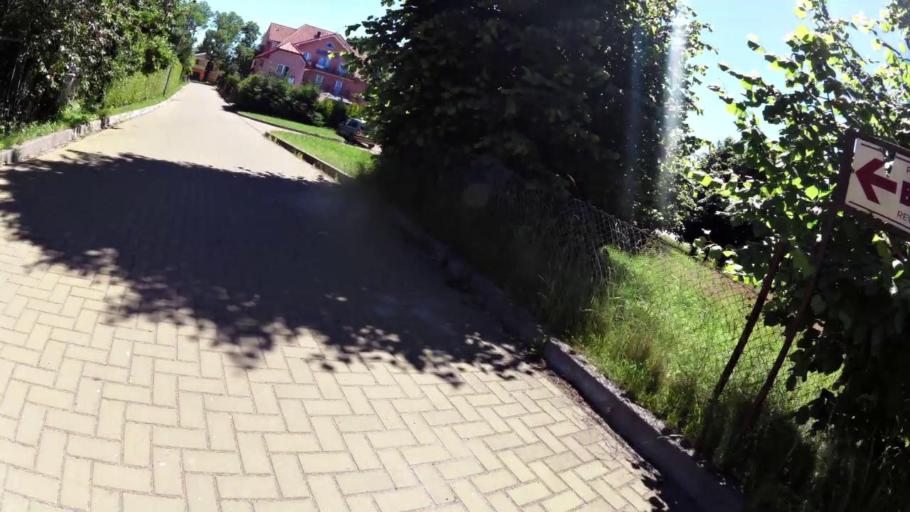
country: PL
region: West Pomeranian Voivodeship
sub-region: Powiat gryficki
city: Rewal
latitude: 54.0795
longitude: 15.0080
